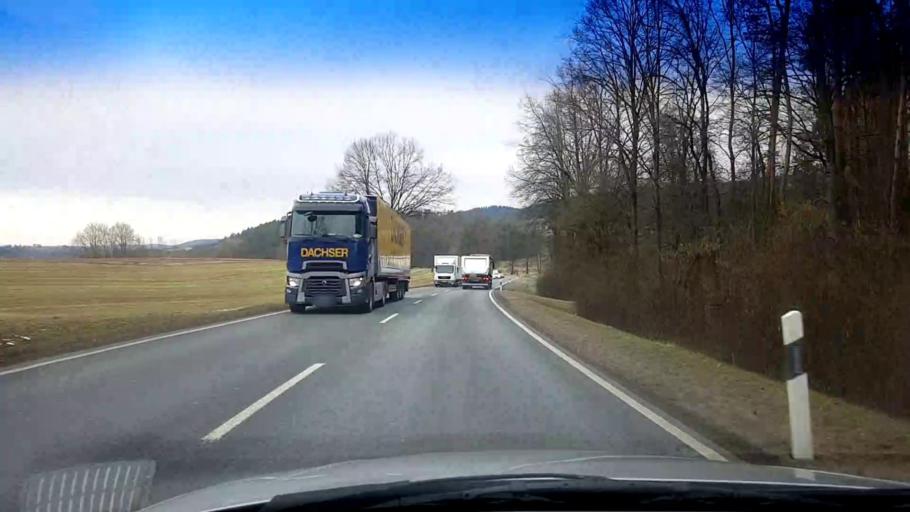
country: DE
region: Bavaria
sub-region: Upper Franconia
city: Neudrossenfeld
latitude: 50.0470
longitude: 11.4835
